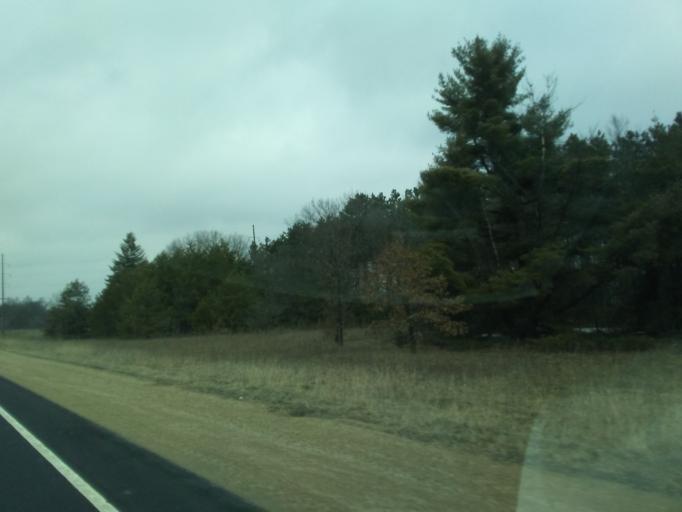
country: US
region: Wisconsin
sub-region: Sauk County
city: Spring Green
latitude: 43.1975
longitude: -90.2363
